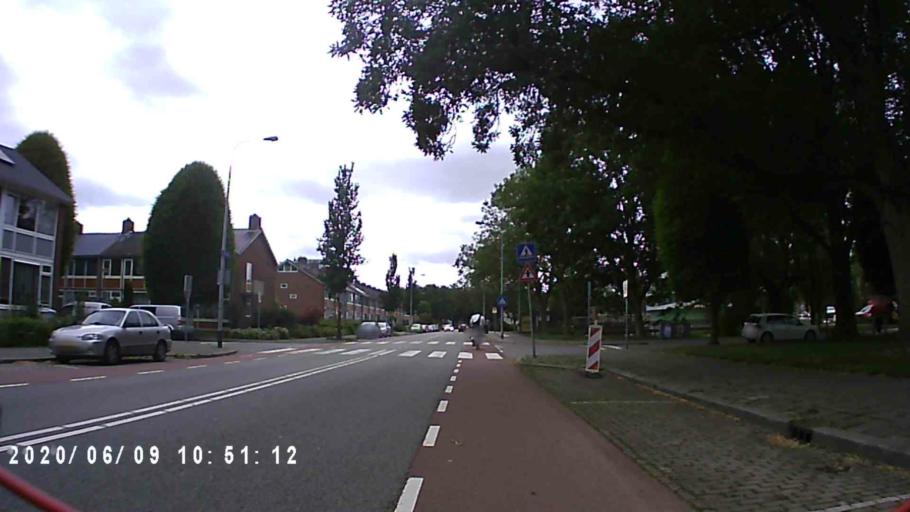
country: NL
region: Groningen
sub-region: Gemeente Groningen
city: Korrewegwijk
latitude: 53.2359
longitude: 6.5552
